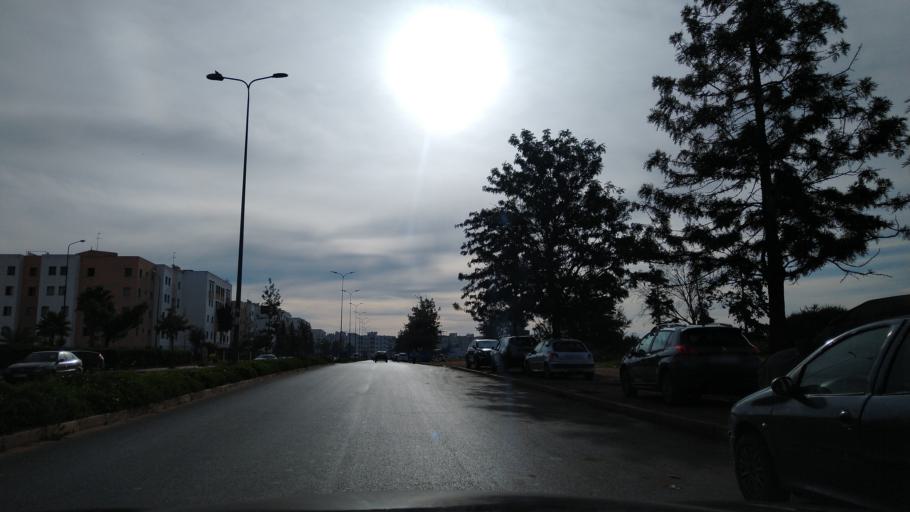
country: MA
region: Rabat-Sale-Zemmour-Zaer
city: Sale
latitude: 33.9915
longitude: -6.7422
